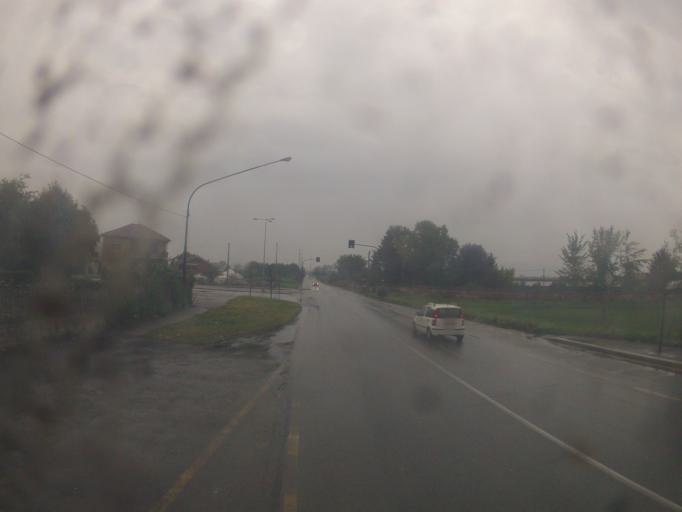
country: IT
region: Piedmont
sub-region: Provincia di Torino
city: La Loggia
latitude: 44.9429
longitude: 7.6701
